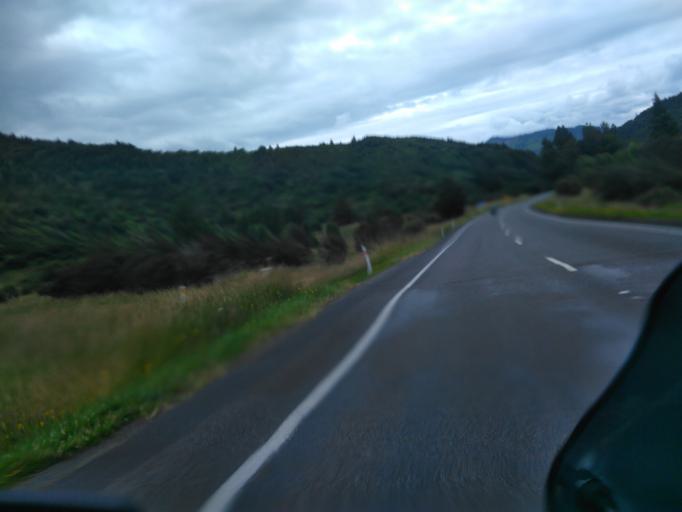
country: NZ
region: Bay of Plenty
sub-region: Opotiki District
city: Opotiki
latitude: -38.2322
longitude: 177.3116
